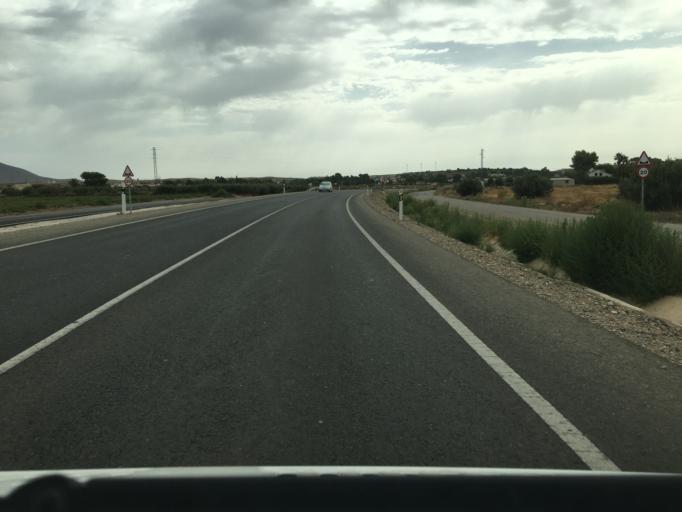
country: ES
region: Andalusia
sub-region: Provincia de Almeria
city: Huercal-Overa
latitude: 37.4169
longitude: -1.8887
